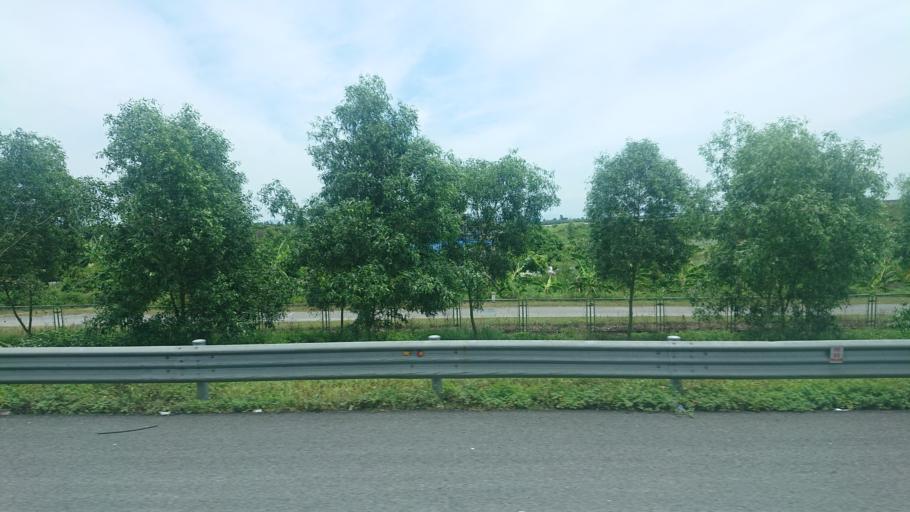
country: VN
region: Hai Phong
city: An Lao
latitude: 20.8185
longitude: 106.4835
